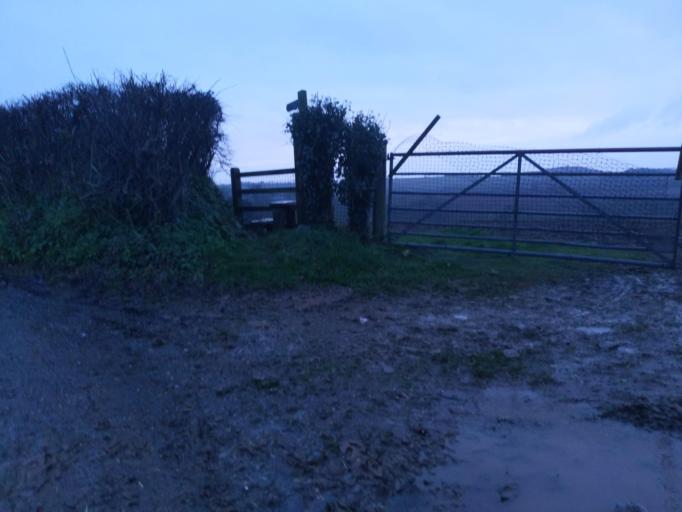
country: GB
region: England
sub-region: Devon
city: Yealmpton
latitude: 50.3365
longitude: -4.0149
